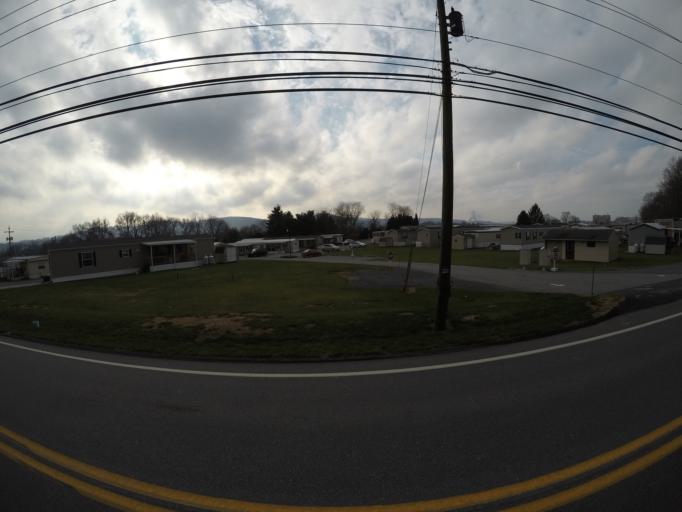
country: US
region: Pennsylvania
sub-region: Lancaster County
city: Marietta
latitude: 40.0623
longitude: -76.5688
